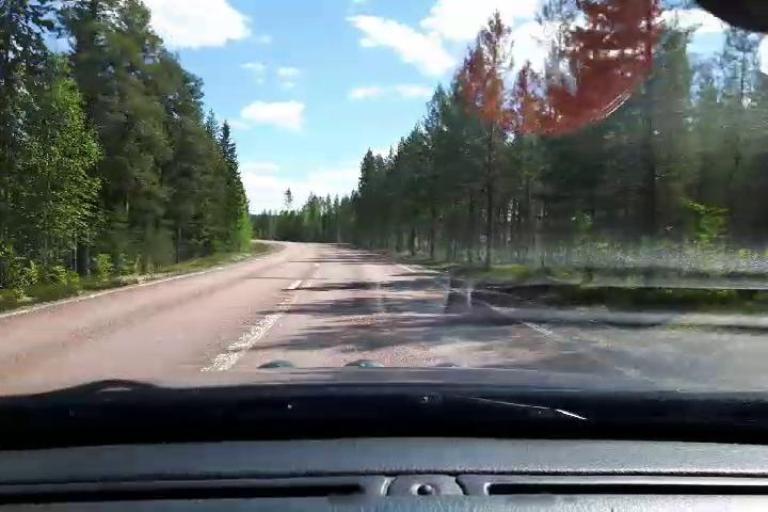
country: SE
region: Gaevleborg
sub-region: Ljusdals Kommun
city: Farila
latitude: 61.9023
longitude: 15.6401
